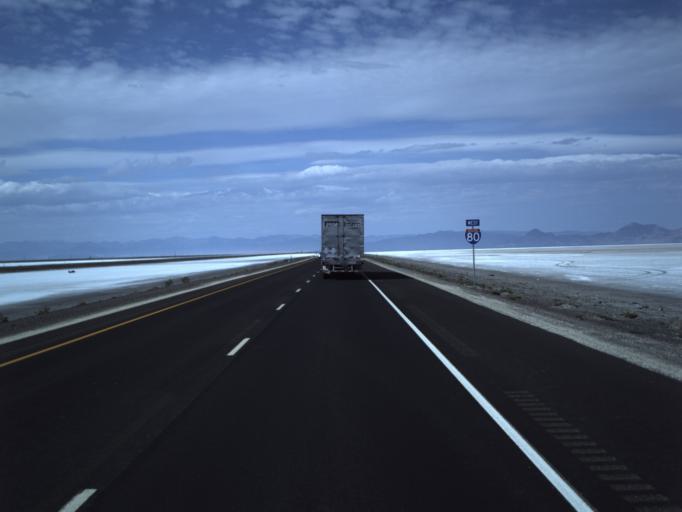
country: US
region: Utah
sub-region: Tooele County
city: Wendover
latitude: 40.7352
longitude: -113.6519
